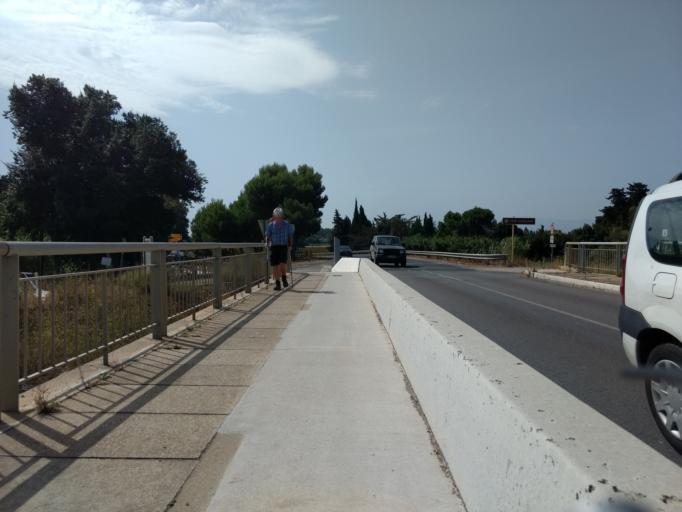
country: FR
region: Languedoc-Roussillon
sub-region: Departement des Pyrenees-Orientales
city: Saint-Laurent-de-la-Salanque
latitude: 42.7636
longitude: 2.9870
